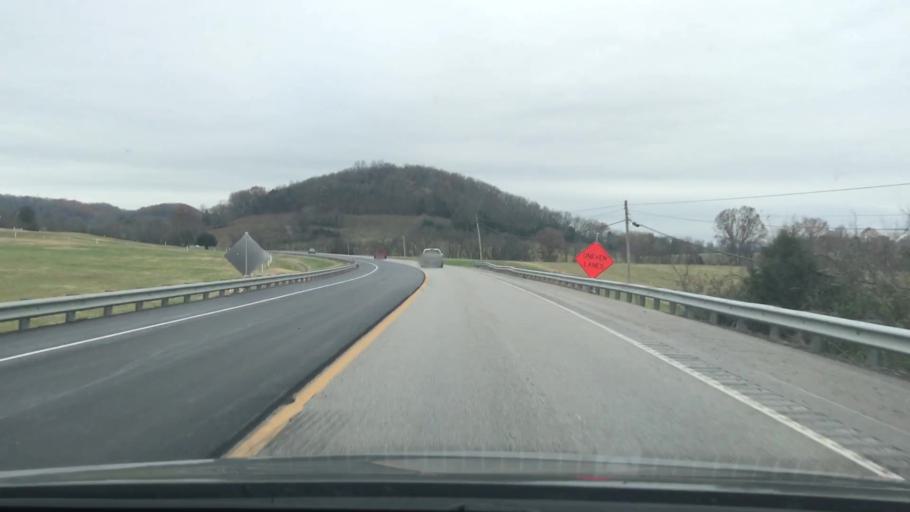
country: US
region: Tennessee
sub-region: Smith County
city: Carthage
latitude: 36.3079
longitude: -86.0075
